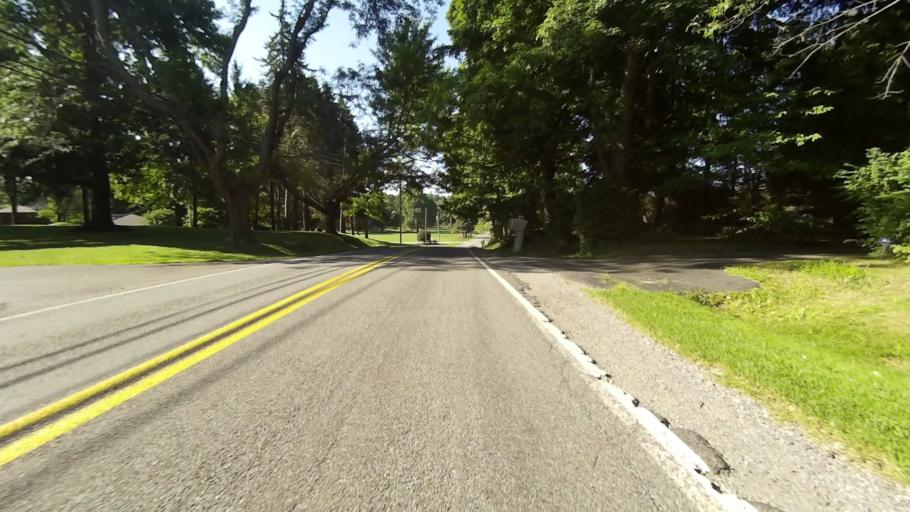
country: US
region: Ohio
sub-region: Portage County
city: Streetsboro
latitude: 41.1964
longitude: -81.3291
